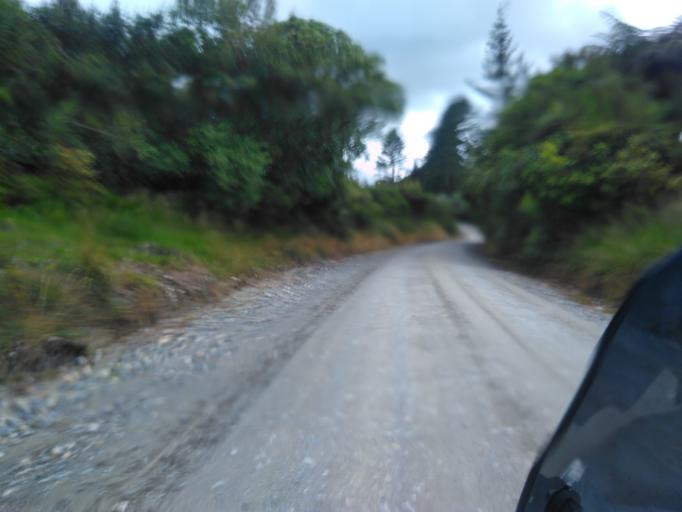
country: NZ
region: Gisborne
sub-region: Gisborne District
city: Gisborne
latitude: -38.2394
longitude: 178.0703
